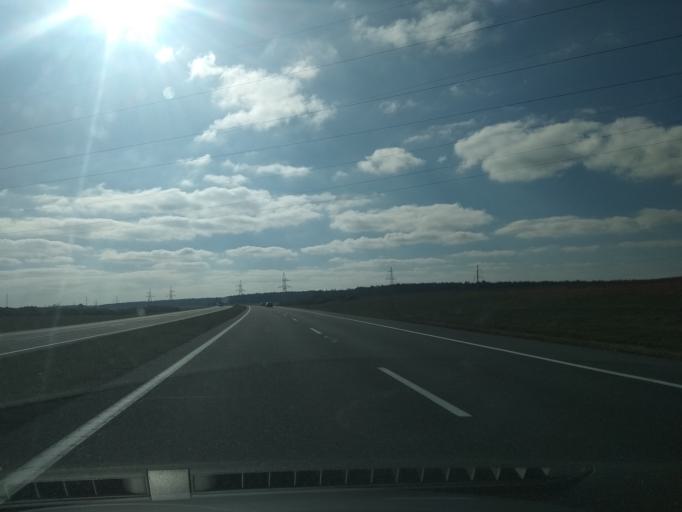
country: BY
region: Brest
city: Baranovichi
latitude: 53.1087
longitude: 25.8904
